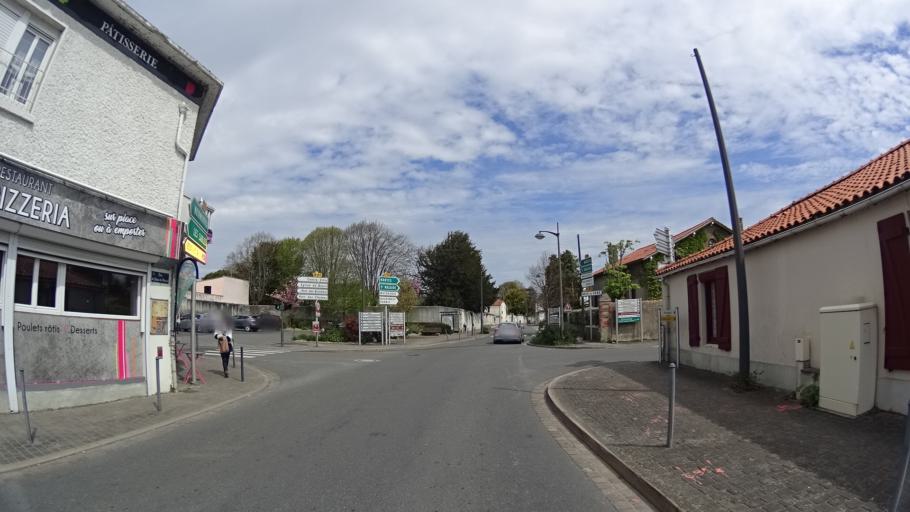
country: FR
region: Pays de la Loire
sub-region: Departement de la Vendee
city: Bouin
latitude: 46.9729
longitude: -1.9968
